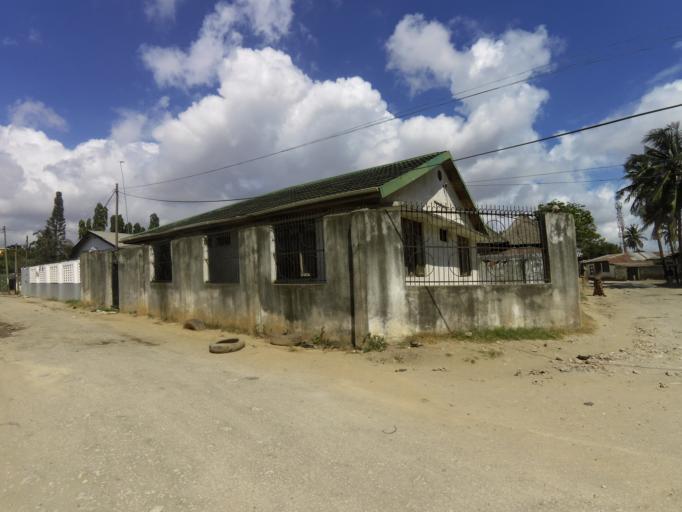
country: TZ
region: Dar es Salaam
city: Magomeni
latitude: -6.7885
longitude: 39.2564
